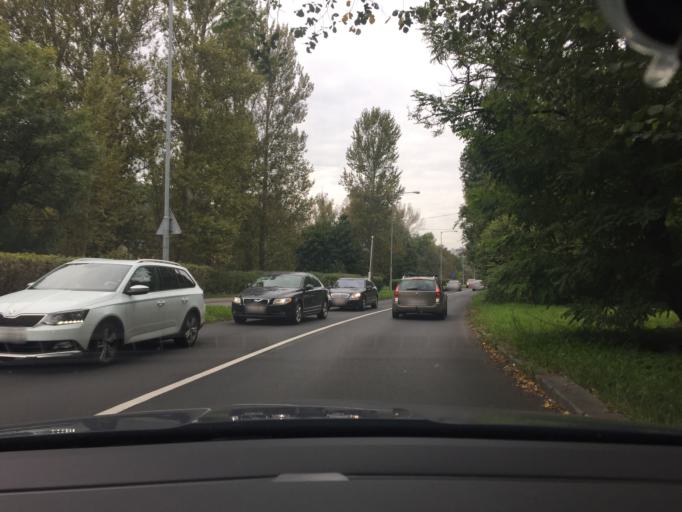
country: CZ
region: Ustecky
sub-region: Okres Usti nad Labem
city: Usti nad Labem
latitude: 50.6459
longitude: 14.0473
